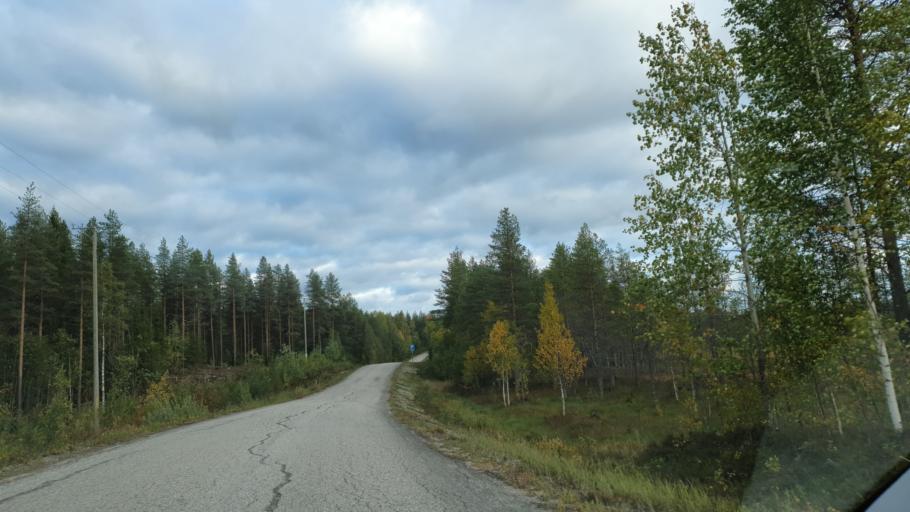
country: FI
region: North Karelia
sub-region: Pielisen Karjala
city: Lieksa
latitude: 63.9146
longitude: 30.1832
